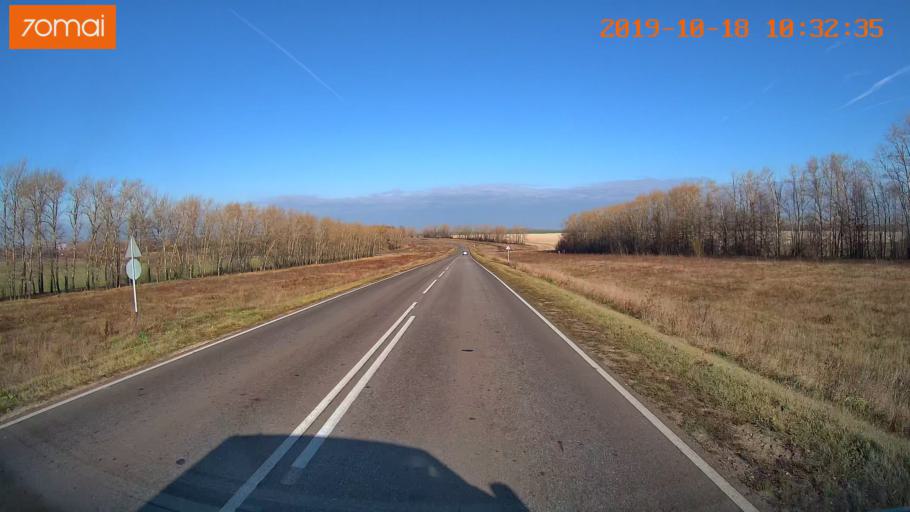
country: RU
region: Tula
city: Kurkino
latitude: 53.4962
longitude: 38.6213
